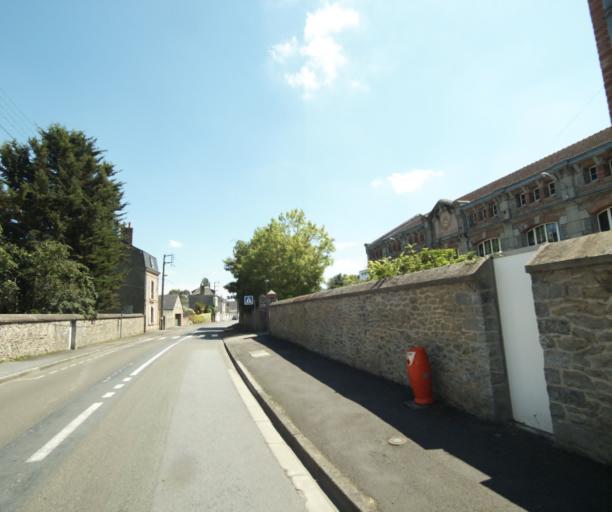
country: FR
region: Pays de la Loire
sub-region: Departement de la Mayenne
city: Laval
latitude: 48.0851
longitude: -0.7739
